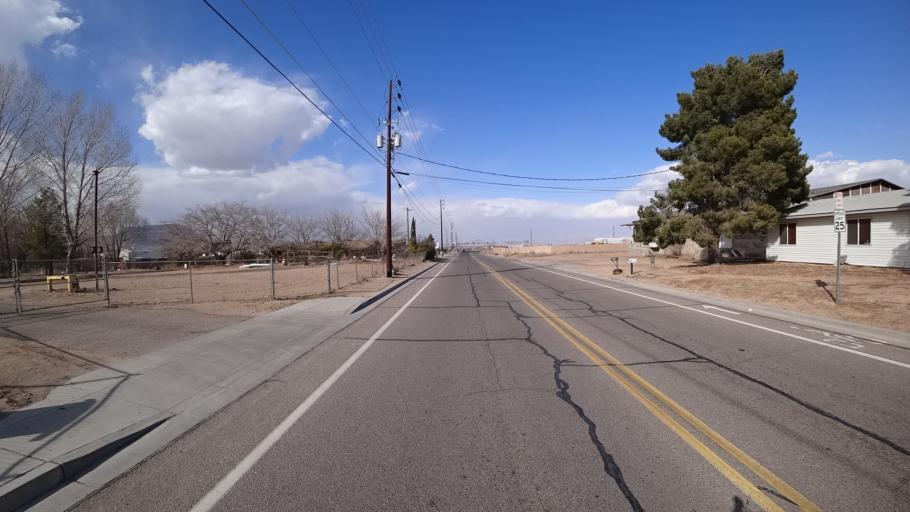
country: US
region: Arizona
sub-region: Mohave County
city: New Kingman-Butler
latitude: 35.2222
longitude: -114.0116
